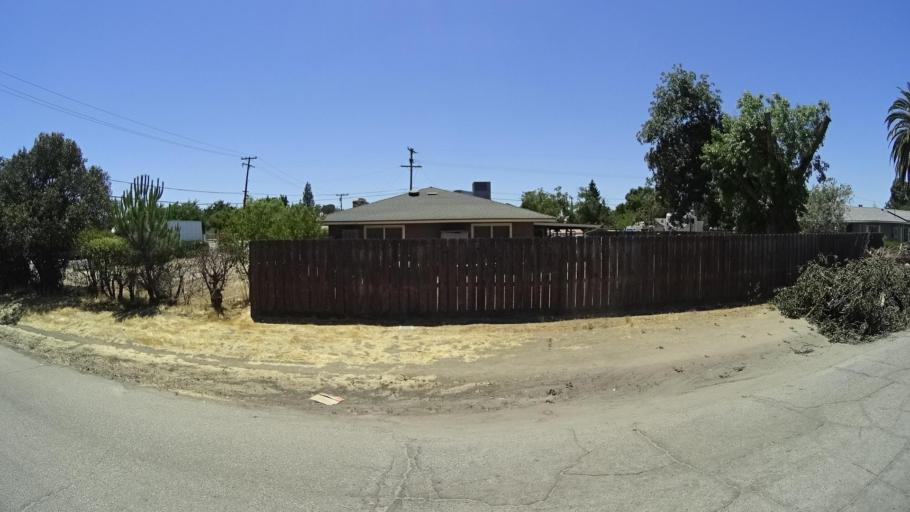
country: US
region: California
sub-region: Fresno County
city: Tarpey Village
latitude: 36.7823
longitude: -119.7410
